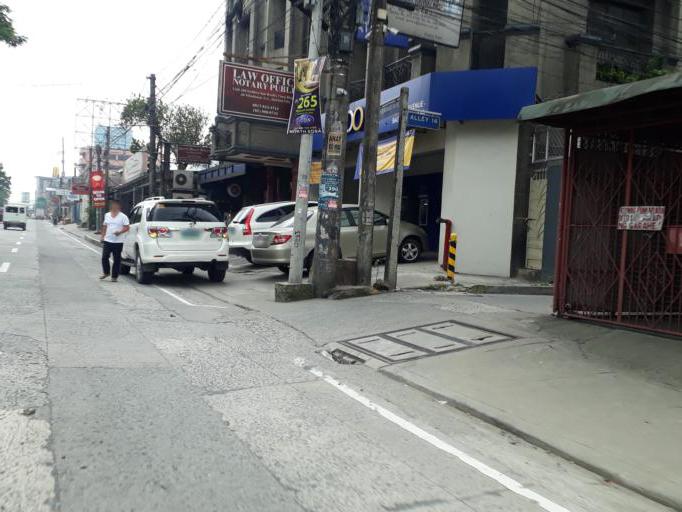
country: PH
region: Calabarzon
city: Bagong Pagasa
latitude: 14.6579
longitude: 121.0359
